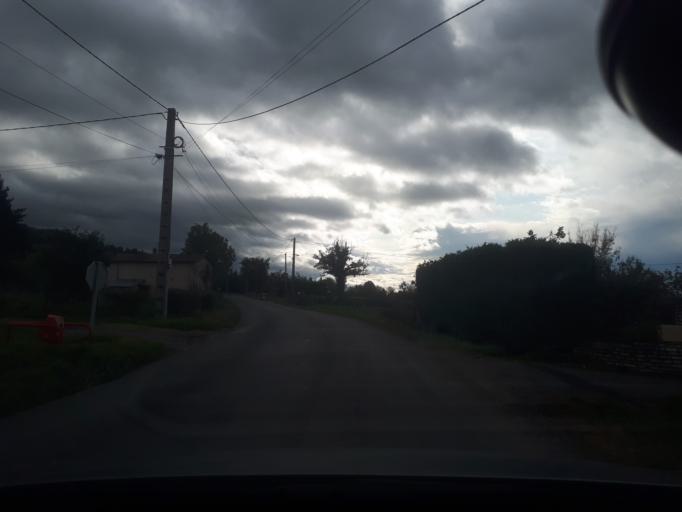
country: FR
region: Rhone-Alpes
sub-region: Departement de la Loire
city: Bellegarde-en-Forez
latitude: 45.6591
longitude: 4.2914
